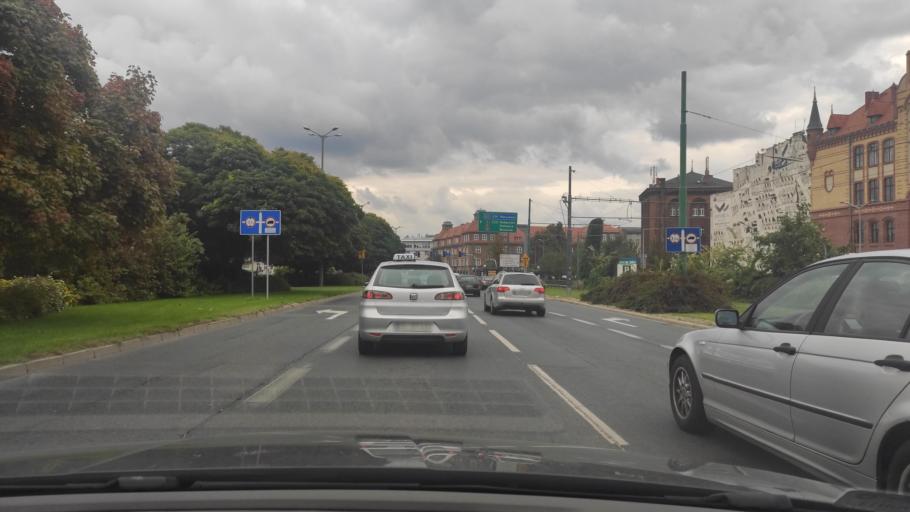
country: PL
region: Greater Poland Voivodeship
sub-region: Poznan
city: Poznan
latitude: 52.4113
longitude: 16.9356
